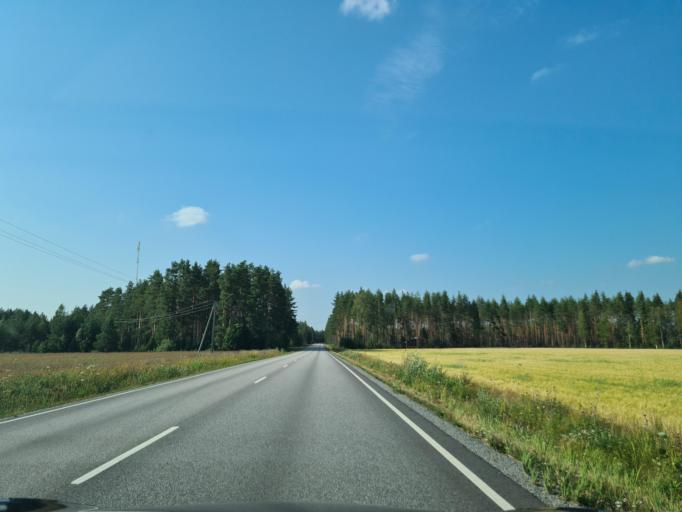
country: FI
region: Satakunta
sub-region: Pohjois-Satakunta
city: Karvia
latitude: 62.0680
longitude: 22.5090
